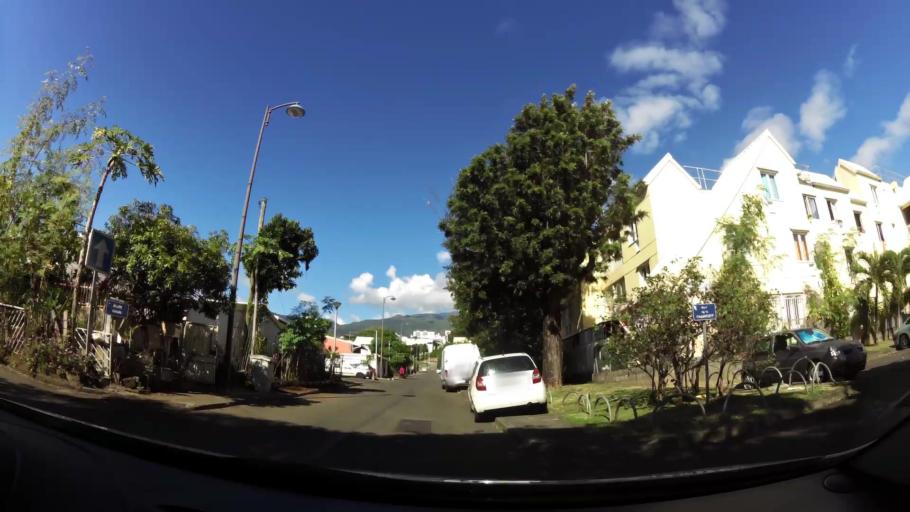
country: RE
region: Reunion
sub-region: Reunion
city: Saint-Denis
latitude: -20.8987
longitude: 55.4846
